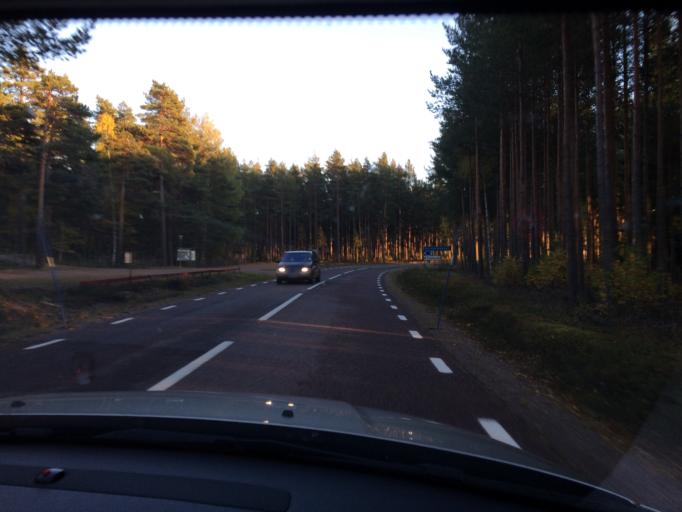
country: SE
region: Gaevleborg
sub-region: Sandvikens Kommun
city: Arsunda
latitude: 60.3310
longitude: 16.7955
